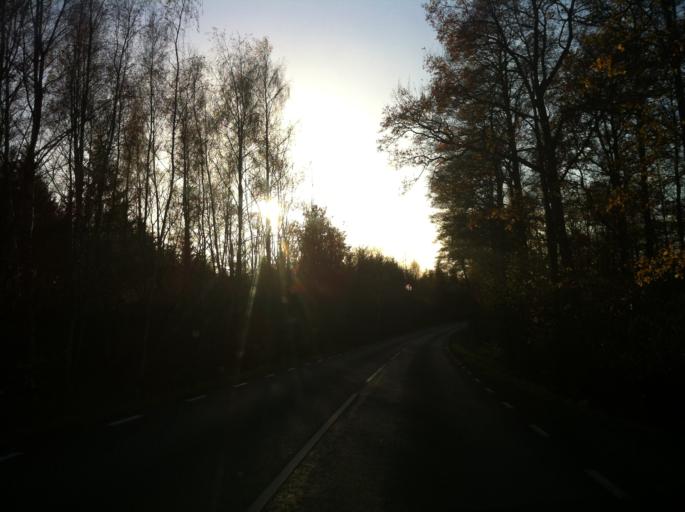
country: SE
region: Skane
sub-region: Ostra Goinge Kommun
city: Knislinge
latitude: 56.1895
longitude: 14.0750
